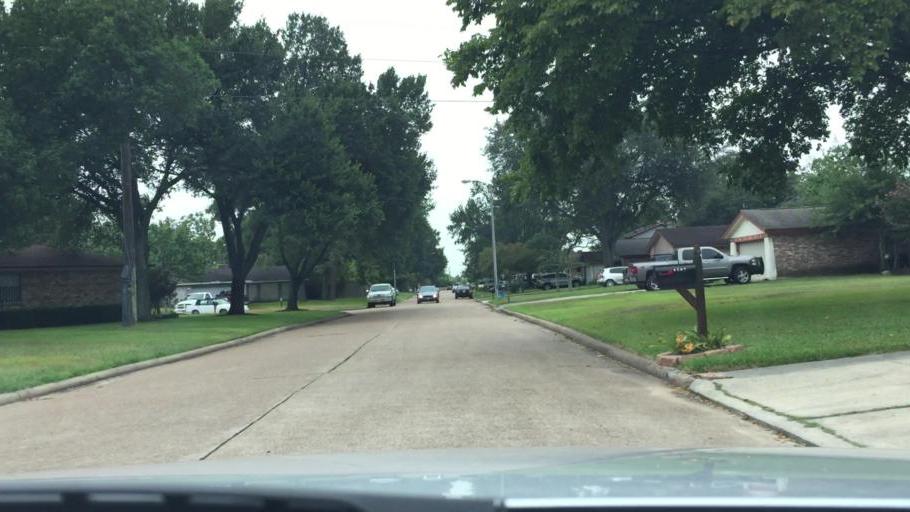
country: US
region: Texas
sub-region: Harris County
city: Hudson
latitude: 29.9046
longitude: -95.5181
